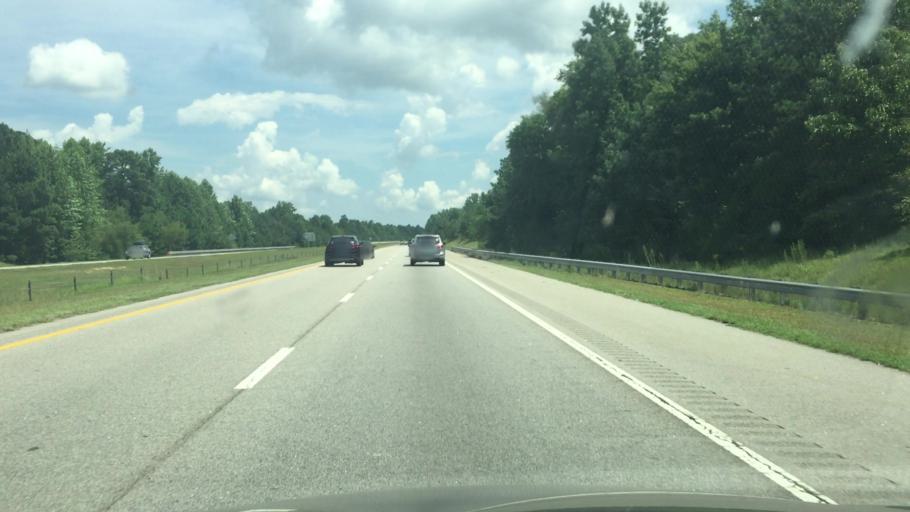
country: US
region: North Carolina
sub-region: Richmond County
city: Ellerbe
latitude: 35.0504
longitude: -79.7610
